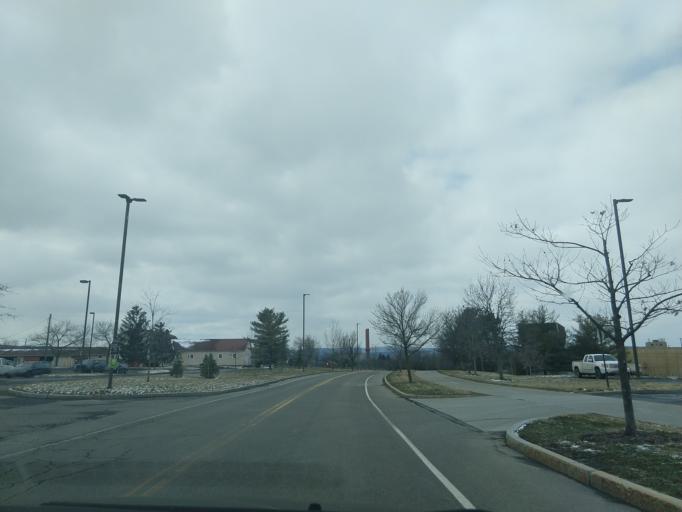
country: US
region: New York
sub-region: Tompkins County
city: East Ithaca
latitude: 42.4458
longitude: -76.4663
